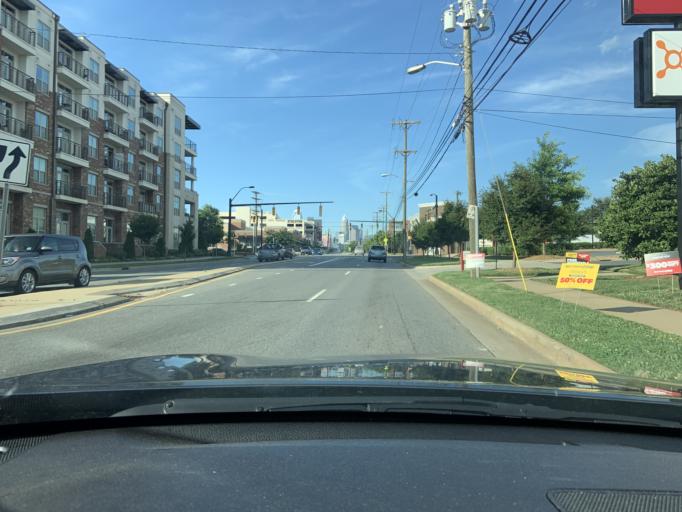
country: US
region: North Carolina
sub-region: Mecklenburg County
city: Charlotte
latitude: 35.2049
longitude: -80.8630
